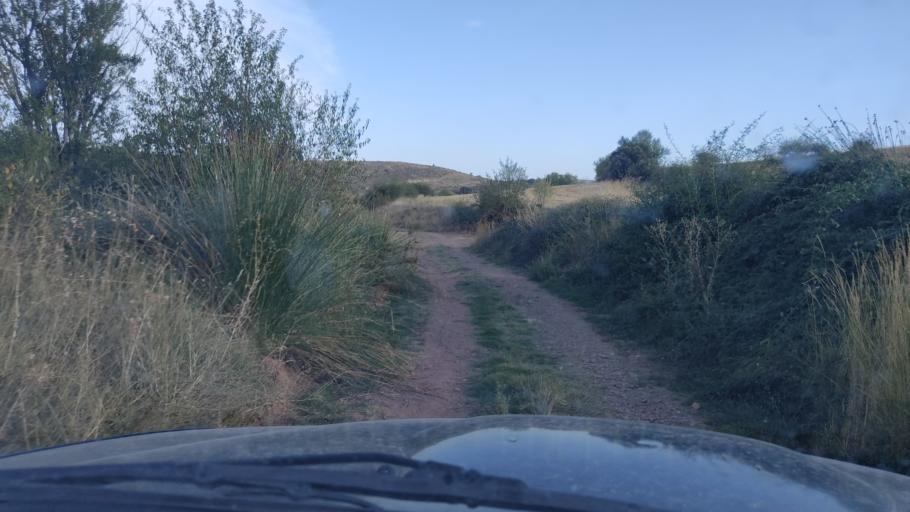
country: ES
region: Aragon
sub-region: Provincia de Teruel
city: Monforte de Moyuela
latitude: 41.0299
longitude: -1.0106
